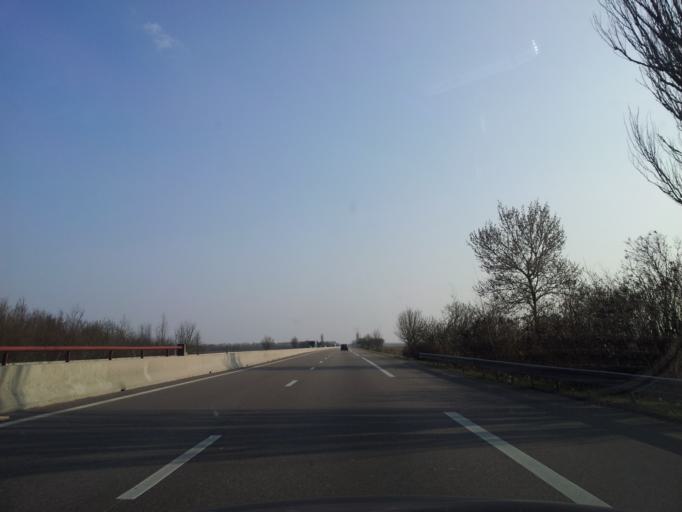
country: FR
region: Alsace
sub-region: Departement du Haut-Rhin
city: Reguisheim
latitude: 47.8925
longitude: 7.3754
